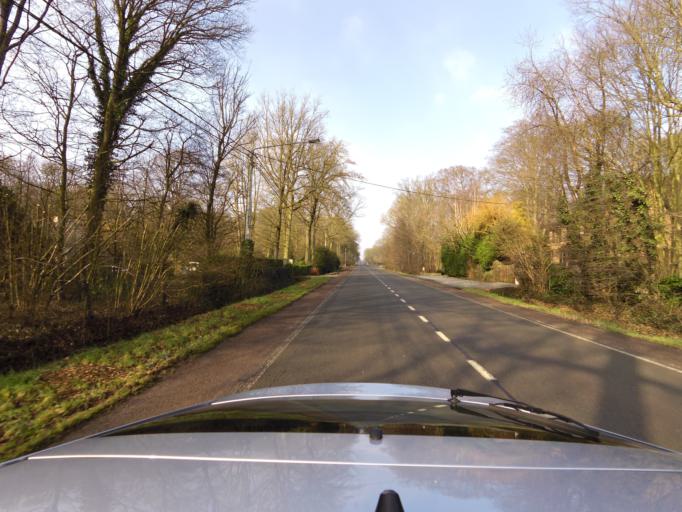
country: BE
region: Wallonia
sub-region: Province du Hainaut
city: Beloeil
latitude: 50.4843
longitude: 3.7457
